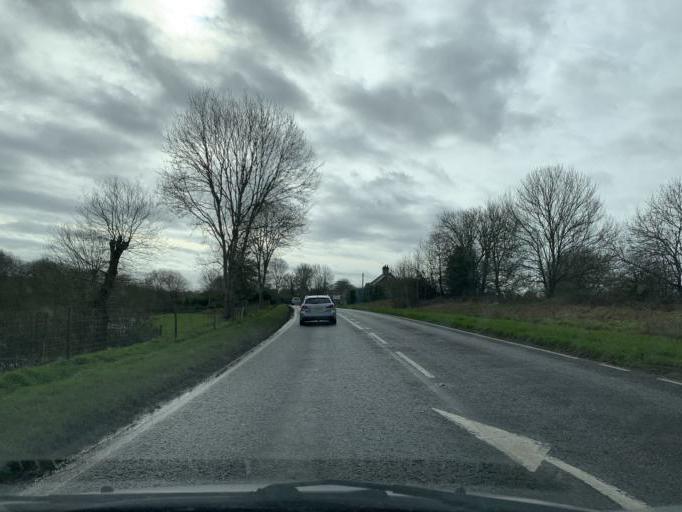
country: GB
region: England
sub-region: Hampshire
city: Fordingbridge
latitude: 50.9453
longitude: -1.7825
